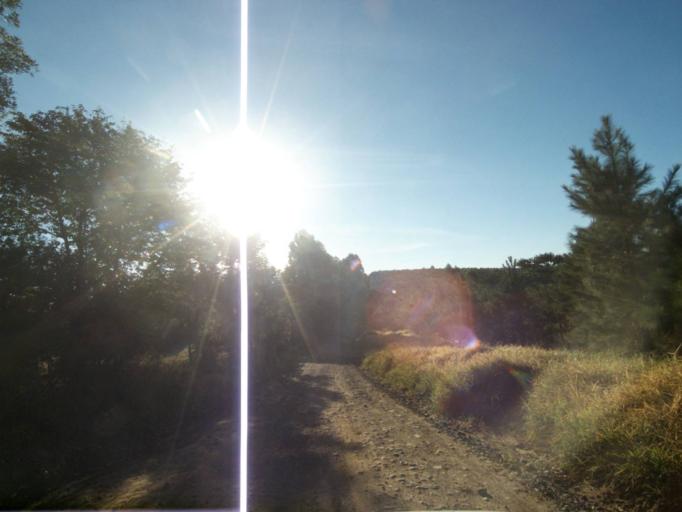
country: BR
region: Parana
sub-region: Tibagi
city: Tibagi
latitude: -24.5240
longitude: -50.5927
